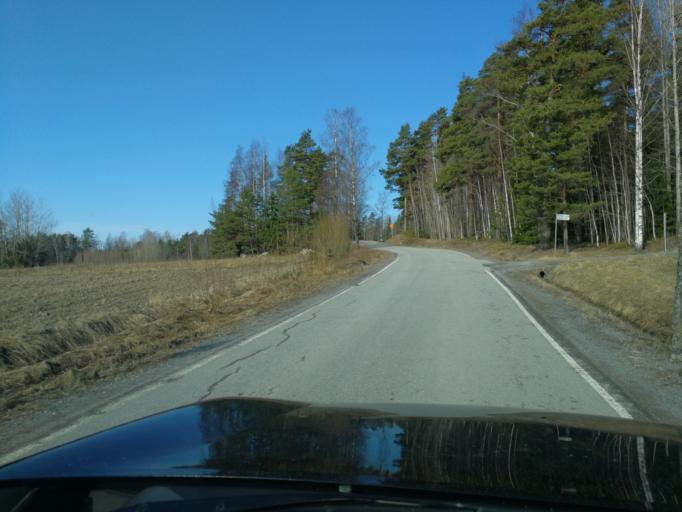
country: FI
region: Uusimaa
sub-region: Raaseporin
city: Inga
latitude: 60.0509
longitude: 24.0450
